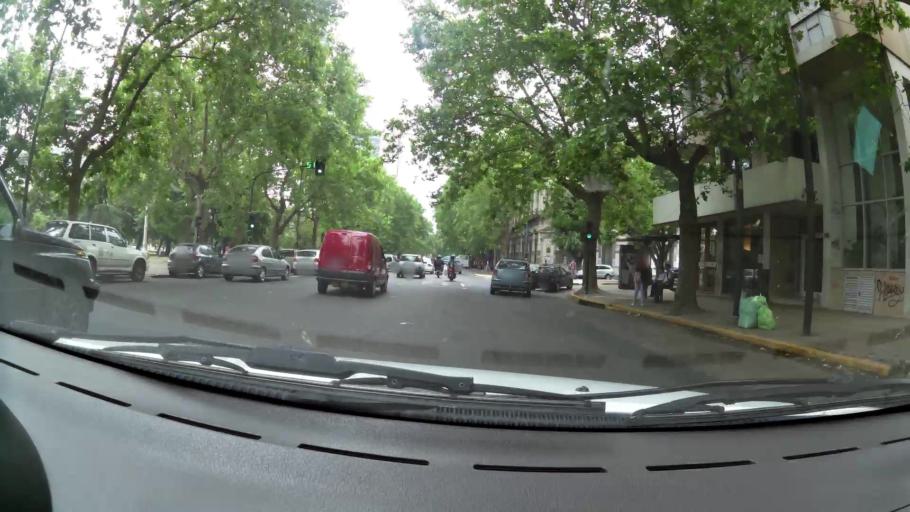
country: AR
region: Buenos Aires
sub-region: Partido de La Plata
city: La Plata
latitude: -34.9226
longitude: -57.9536
